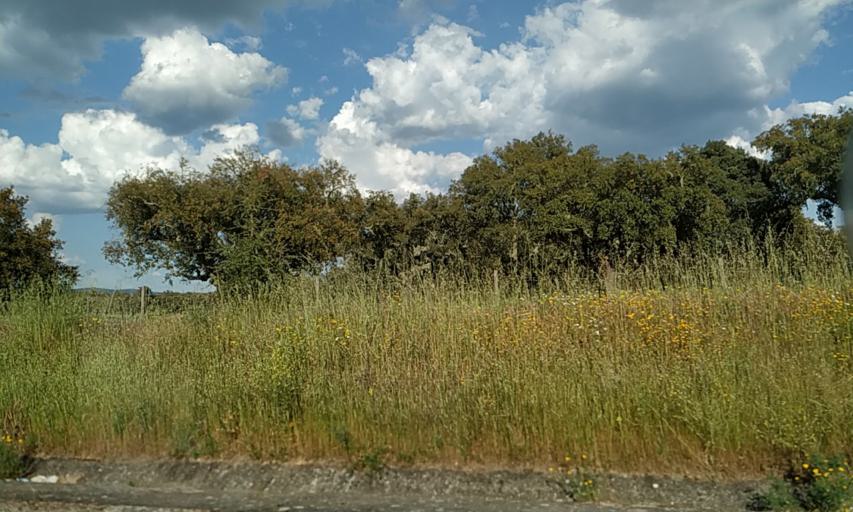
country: PT
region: Portalegre
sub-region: Portalegre
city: Urra
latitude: 39.2288
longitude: -7.4549
